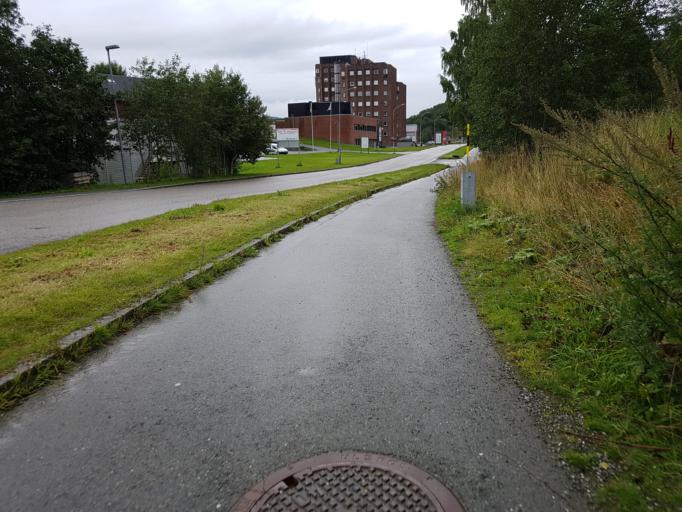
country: NO
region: Sor-Trondelag
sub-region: Trondheim
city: Trondheim
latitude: 63.3901
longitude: 10.4047
